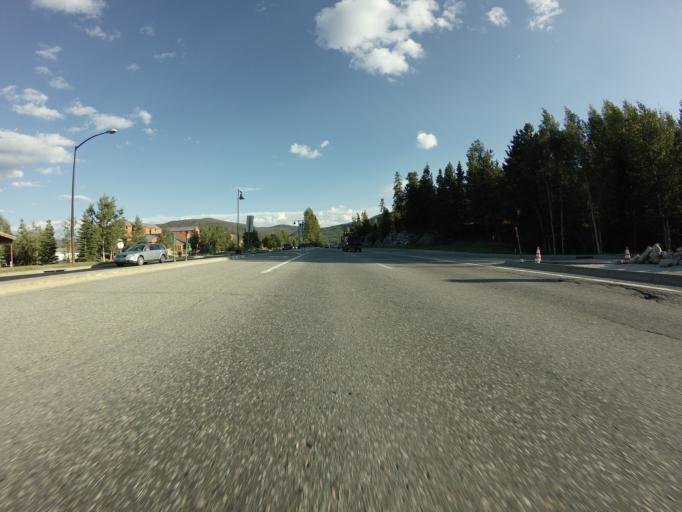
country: US
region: Colorado
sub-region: Summit County
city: Frisco
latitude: 39.5840
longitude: -106.0941
